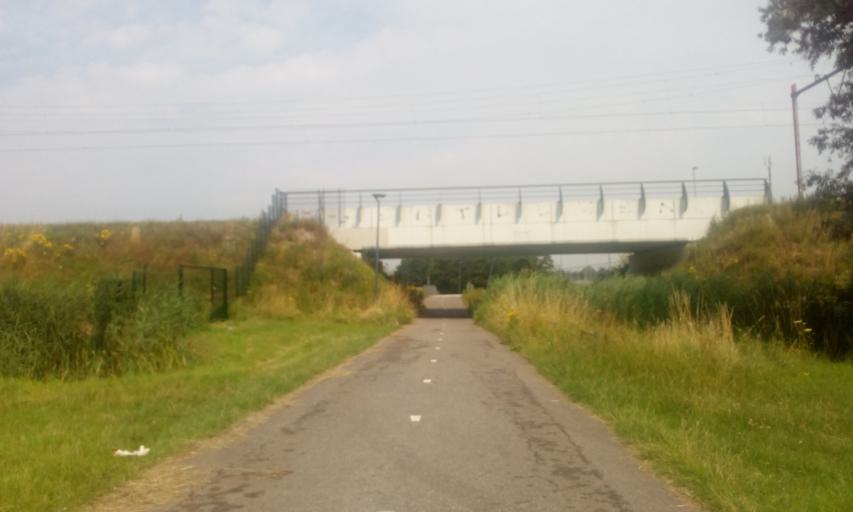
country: NL
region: South Holland
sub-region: Gemeente Capelle aan den IJssel
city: Capelle aan den IJssel
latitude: 51.9572
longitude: 4.6009
